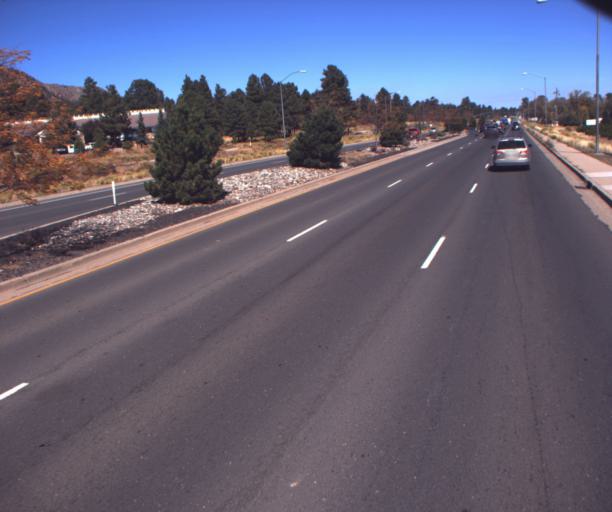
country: US
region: Arizona
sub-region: Coconino County
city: Flagstaff
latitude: 35.2274
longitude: -111.5800
